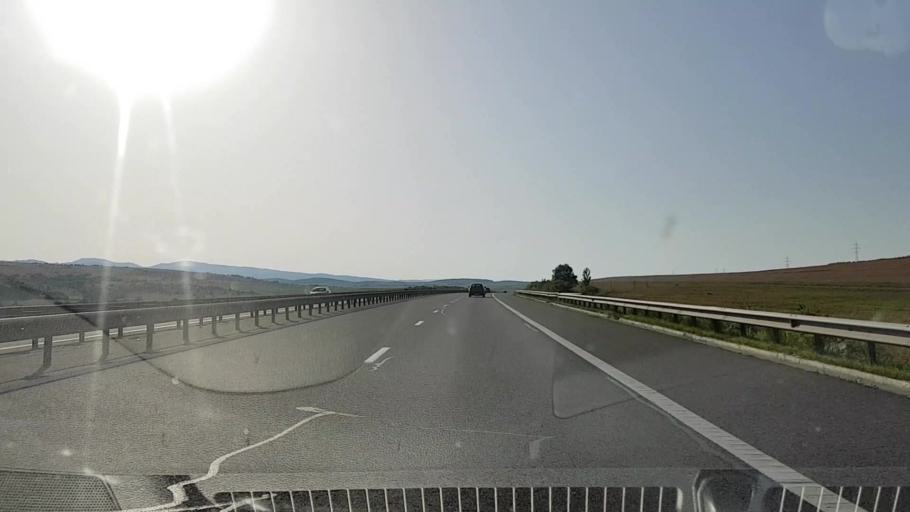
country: RO
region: Cluj
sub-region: Comuna Ciurila
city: Ciurila
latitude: 46.6353
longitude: 23.5341
